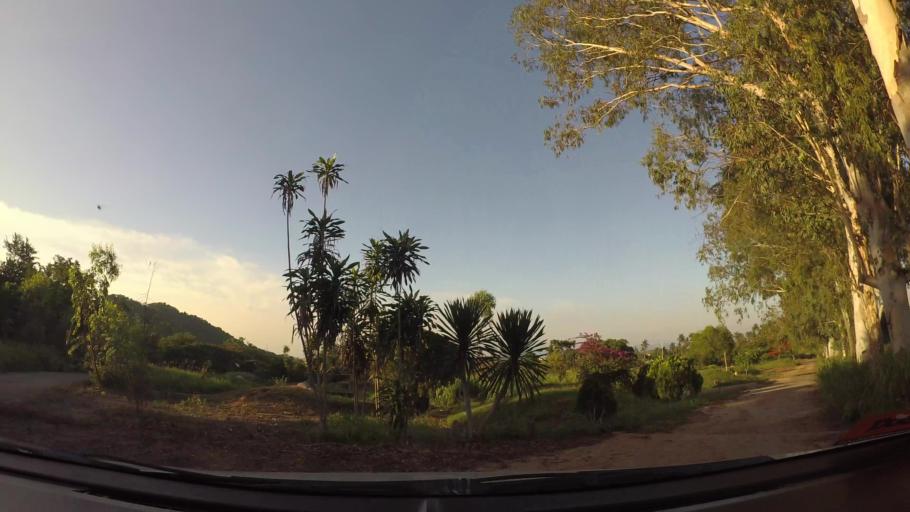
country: TH
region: Chon Buri
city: Si Racha
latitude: 13.1345
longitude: 100.9283
